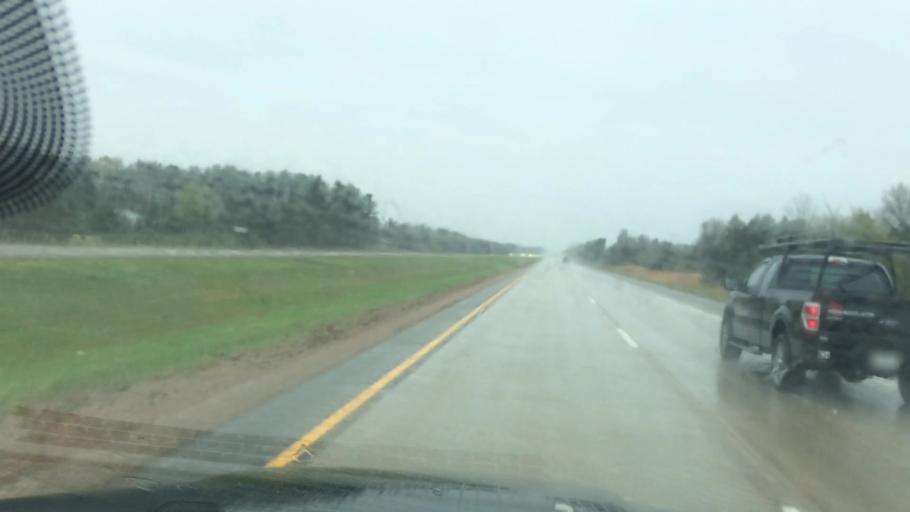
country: US
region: Wisconsin
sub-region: Portage County
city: Stevens Point
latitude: 44.6264
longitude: -89.6322
